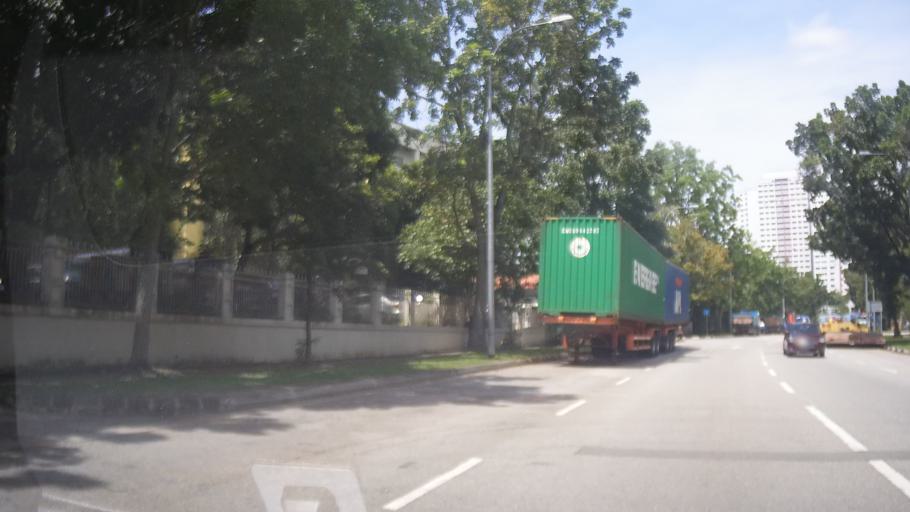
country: MY
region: Johor
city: Johor Bahru
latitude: 1.4071
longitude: 103.7525
